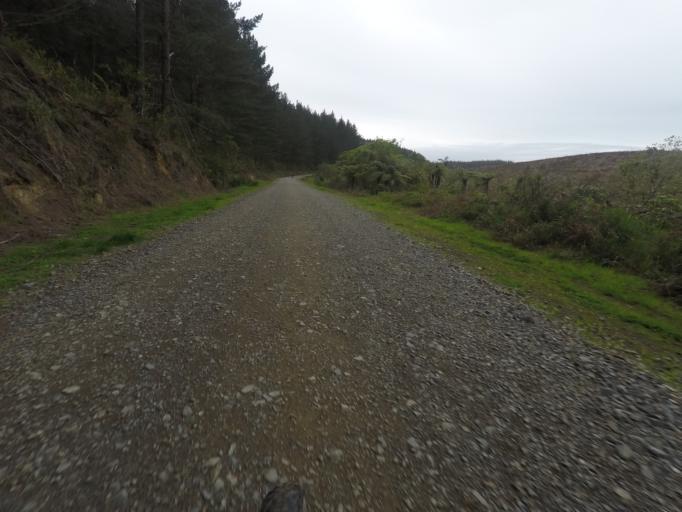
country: NZ
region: Auckland
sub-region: Auckland
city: Muriwai Beach
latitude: -36.7506
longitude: 174.5752
